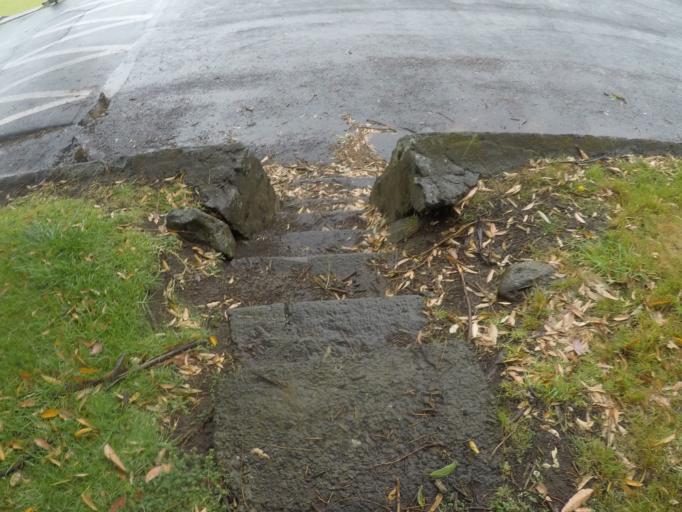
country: NZ
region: Auckland
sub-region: Auckland
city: Auckland
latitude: -36.8638
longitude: 174.7744
